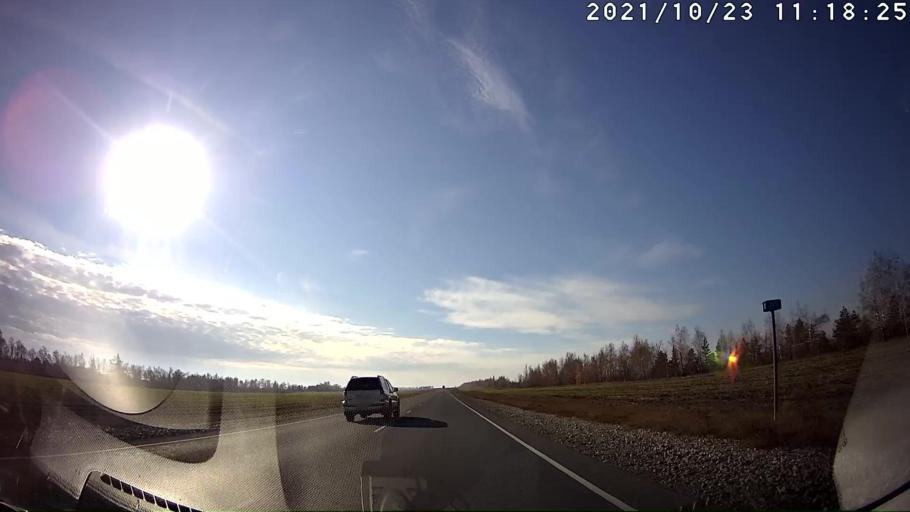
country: RU
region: Saratov
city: Kamenskiy
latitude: 50.8967
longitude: 45.5927
